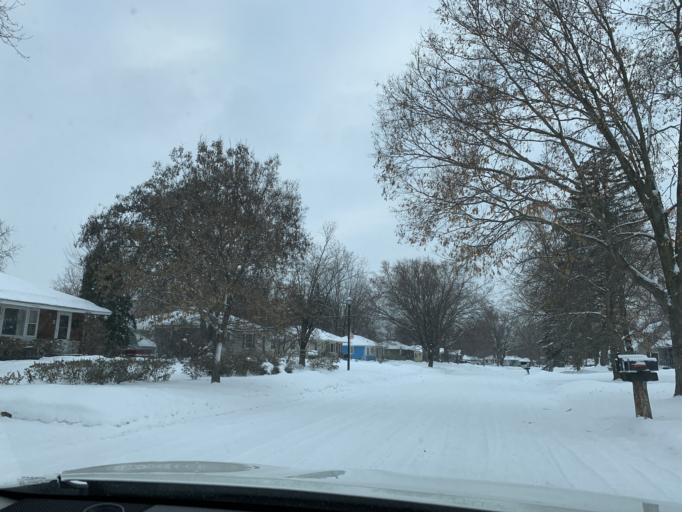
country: US
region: Minnesota
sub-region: Anoka County
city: Blaine
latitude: 45.1739
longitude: -93.2857
